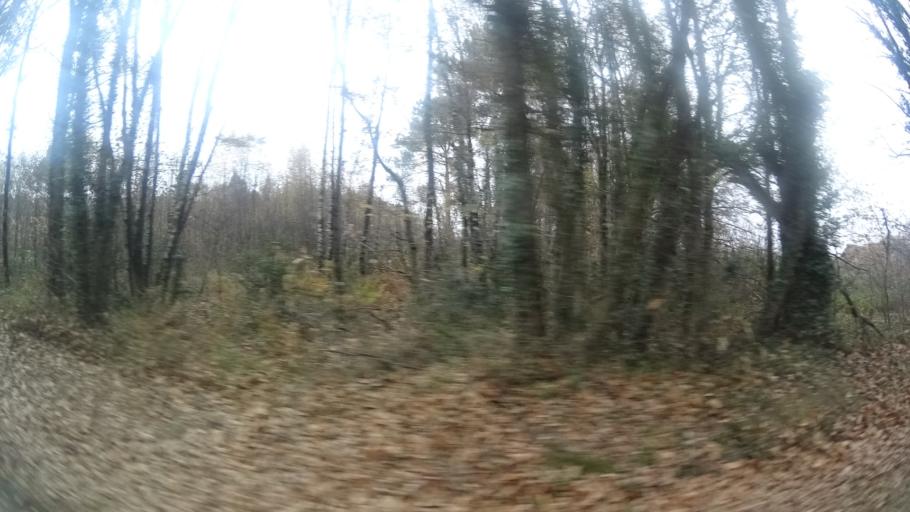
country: FR
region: Brittany
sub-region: Departement d'Ille-et-Vilaine
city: Sainte-Marie
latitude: 47.7081
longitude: -2.0307
